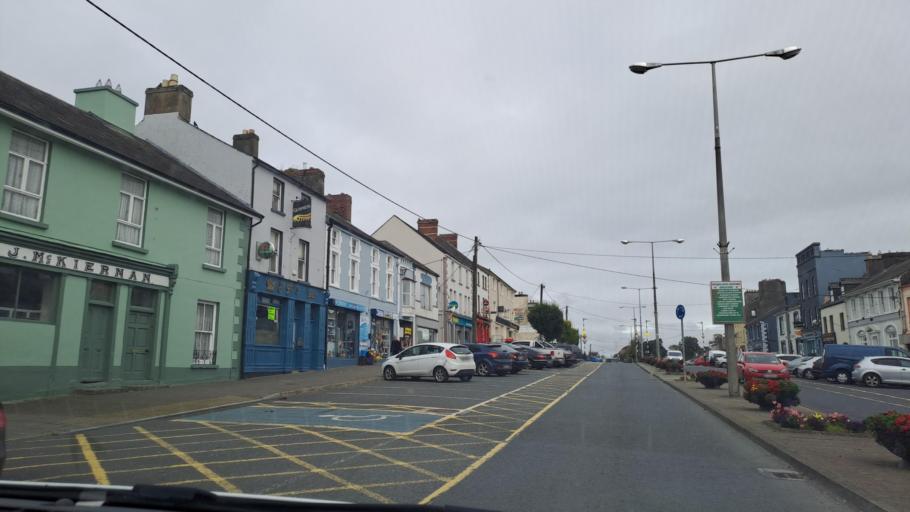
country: IE
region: Ulster
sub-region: An Cabhan
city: Kingscourt
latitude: 53.9055
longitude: -6.8048
